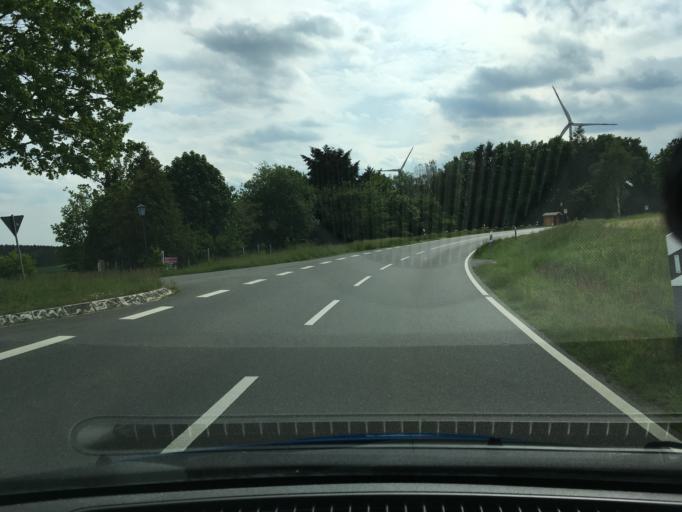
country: DE
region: Lower Saxony
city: Betzendorf
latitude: 53.1061
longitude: 10.2995
